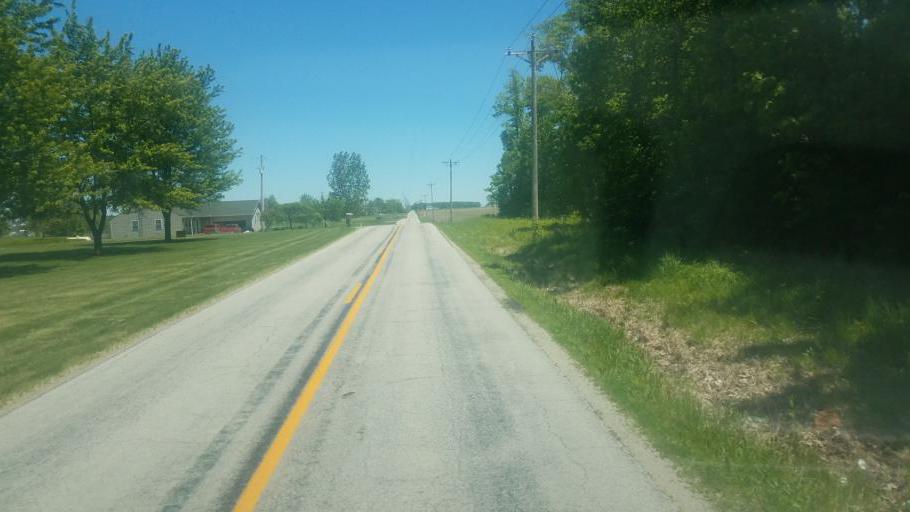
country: US
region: Ohio
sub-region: Miami County
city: Covington
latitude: 40.2270
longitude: -84.3451
